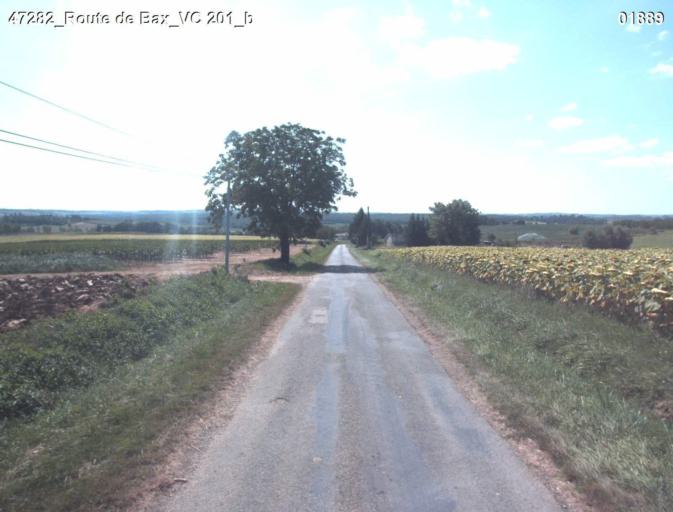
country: FR
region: Aquitaine
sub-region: Departement du Lot-et-Garonne
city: Laplume
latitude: 44.0843
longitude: 0.4992
